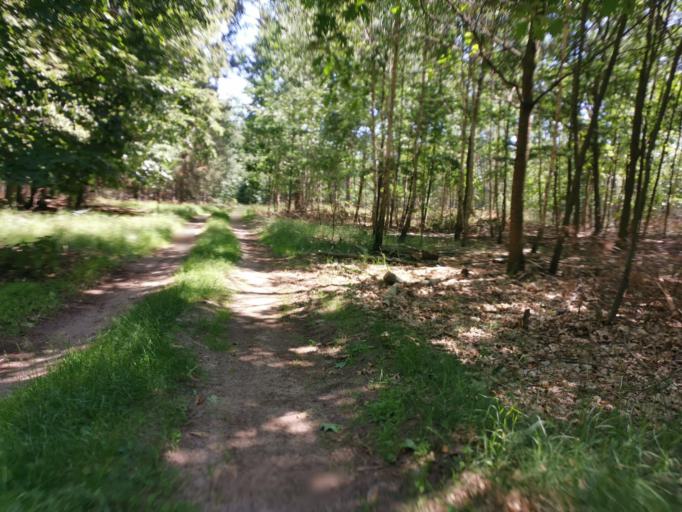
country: CZ
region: South Moravian
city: Vracov
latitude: 48.9468
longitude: 17.2366
